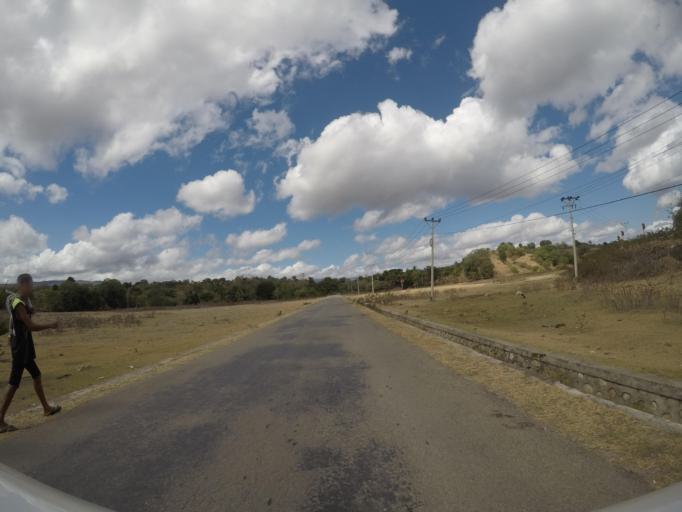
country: TL
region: Lautem
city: Lospalos
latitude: -8.4029
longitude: 126.8307
